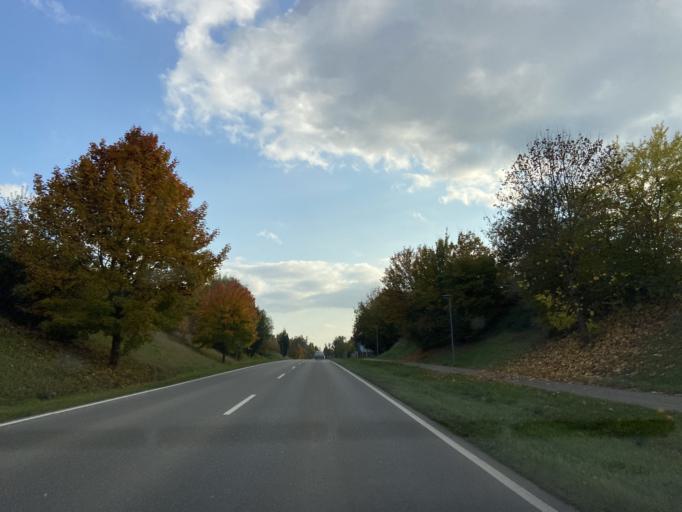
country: DE
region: Baden-Wuerttemberg
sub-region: Tuebingen Region
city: Sigmaringen
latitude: 48.0922
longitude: 9.2409
